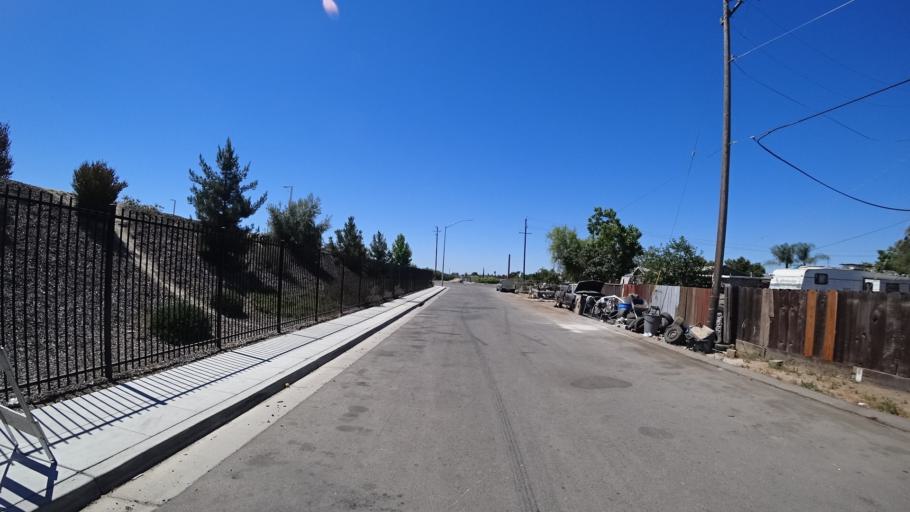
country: US
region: California
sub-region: Fresno County
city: Easton
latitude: 36.6786
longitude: -119.7773
